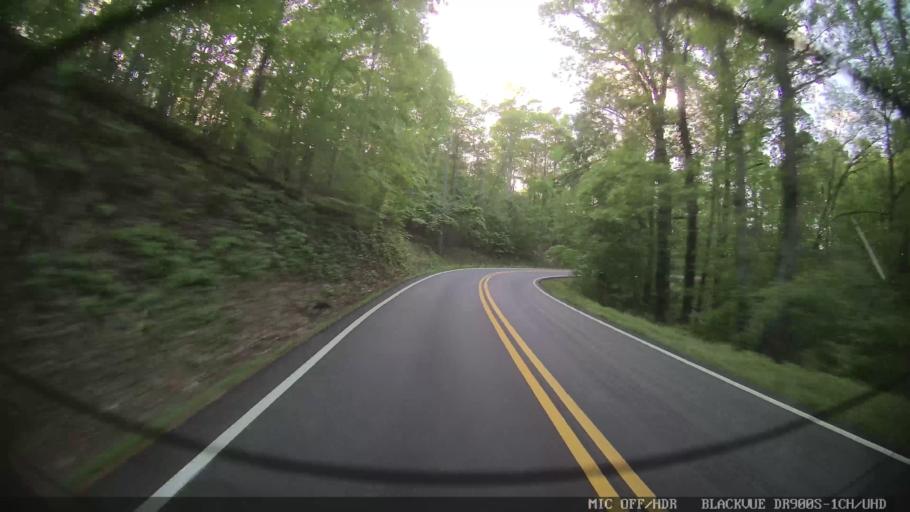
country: US
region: Georgia
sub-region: Bartow County
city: Emerson
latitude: 34.0885
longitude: -84.7663
